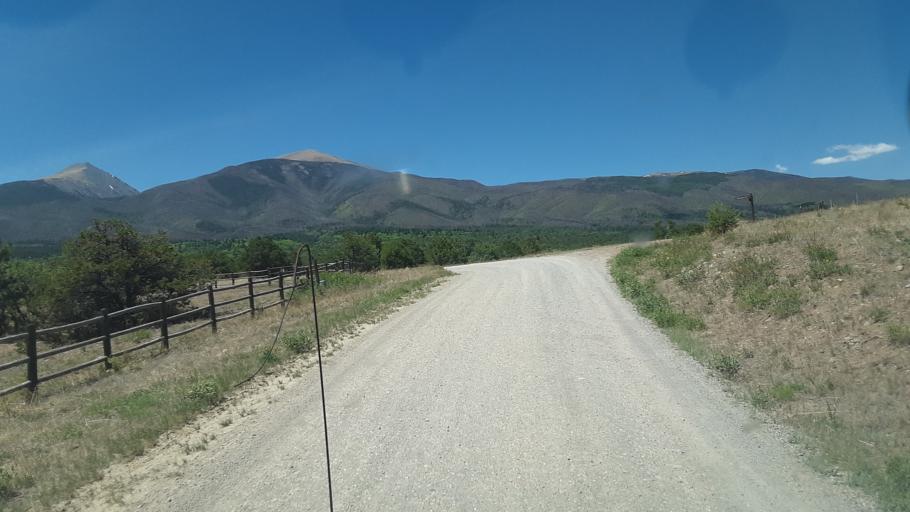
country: US
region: Colorado
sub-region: Custer County
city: Westcliffe
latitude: 38.3072
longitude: -105.6772
